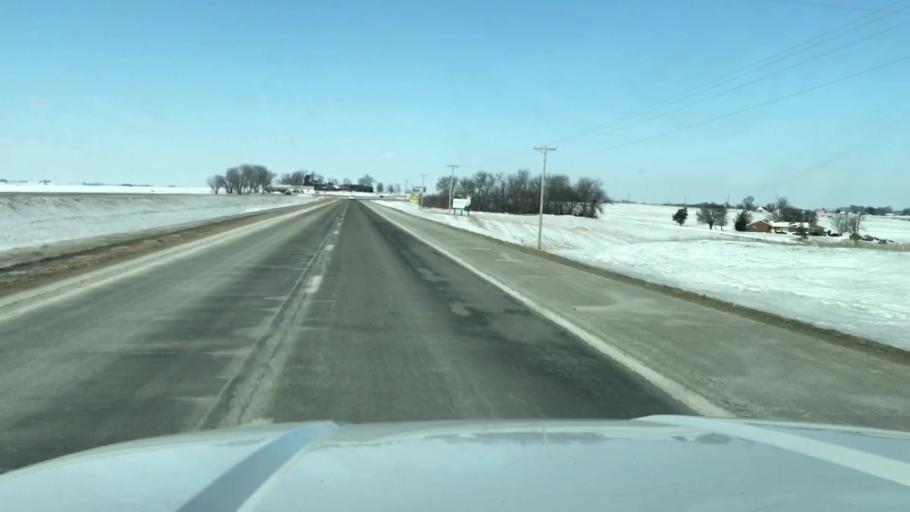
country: US
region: Missouri
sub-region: Nodaway County
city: Maryville
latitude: 40.2743
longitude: -94.8692
